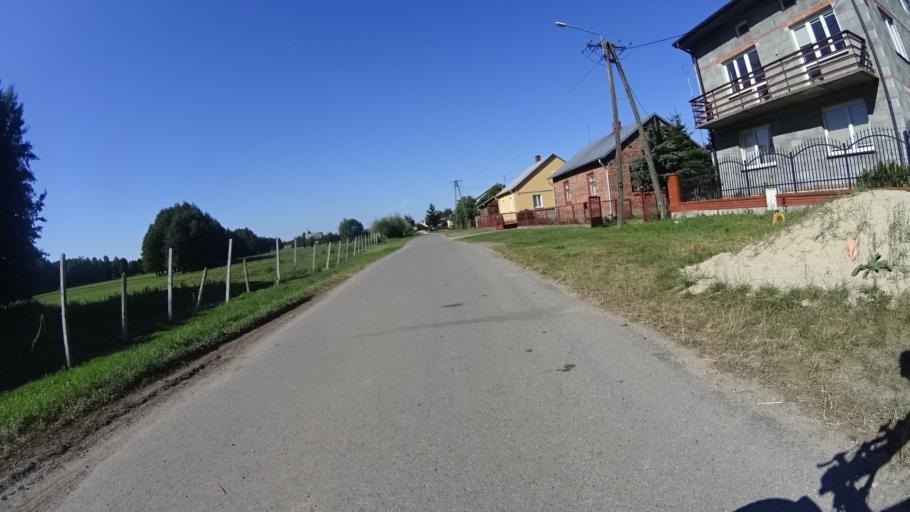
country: PL
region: Masovian Voivodeship
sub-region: Powiat bialobrzeski
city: Wysmierzyce
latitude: 51.6652
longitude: 20.8480
